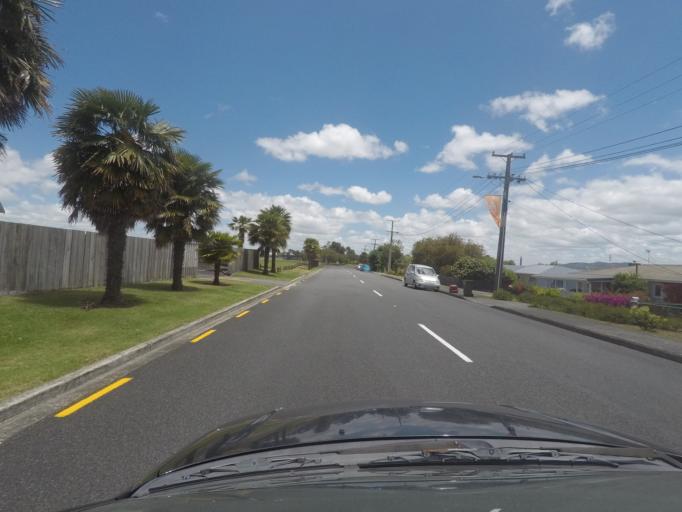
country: NZ
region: Northland
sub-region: Whangarei
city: Whangarei
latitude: -35.7652
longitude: 174.3667
